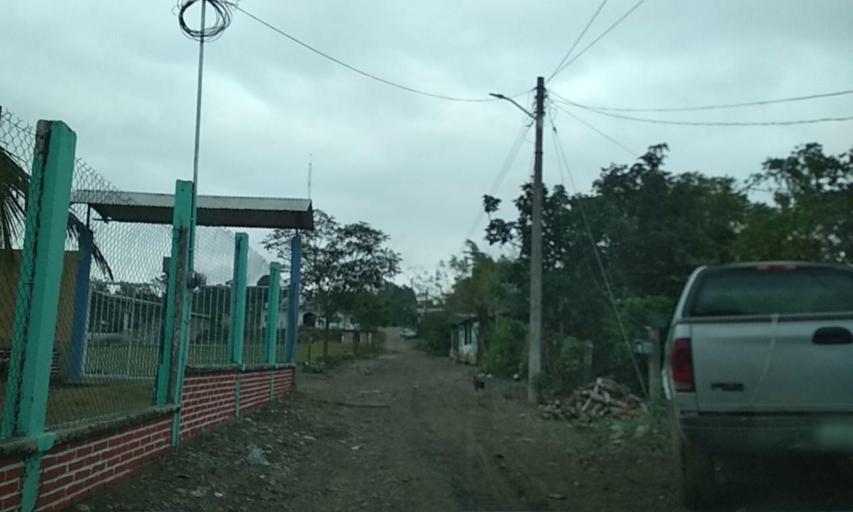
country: MX
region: Veracruz
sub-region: Coatzintla
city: Manuel Maria Contreras
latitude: 20.3582
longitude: -97.5112
